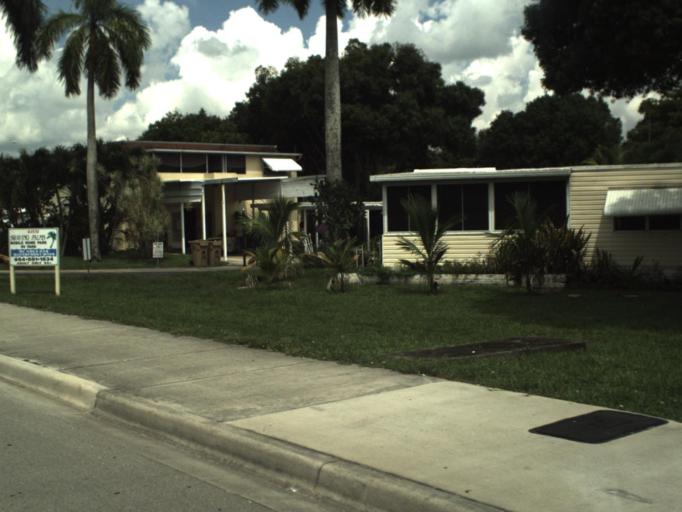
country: US
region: Florida
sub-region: Broward County
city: Davie
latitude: 26.0629
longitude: -80.2100
